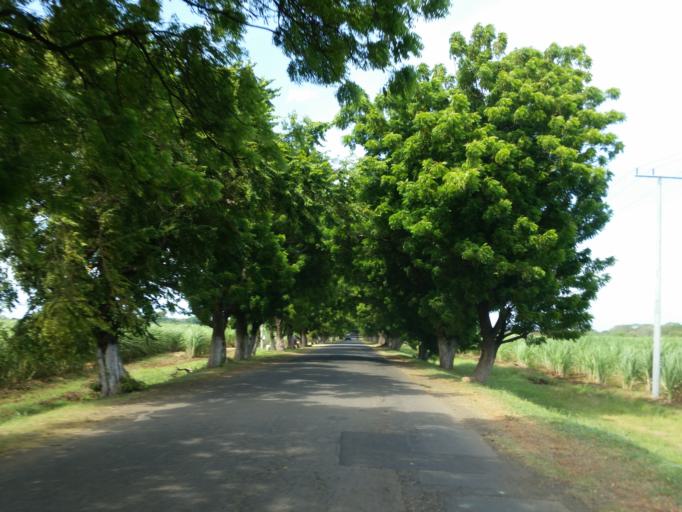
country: NI
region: Managua
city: Masachapa
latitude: 11.7977
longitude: -86.5011
